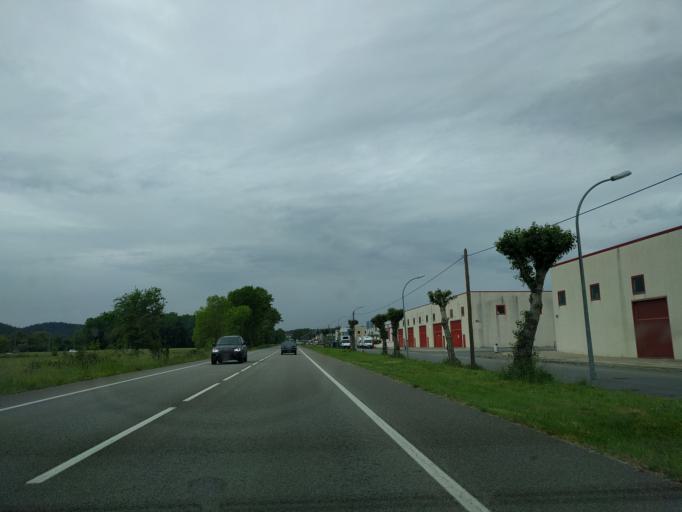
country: ES
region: Catalonia
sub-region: Provincia de Girona
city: Breda
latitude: 41.7217
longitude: 2.5568
